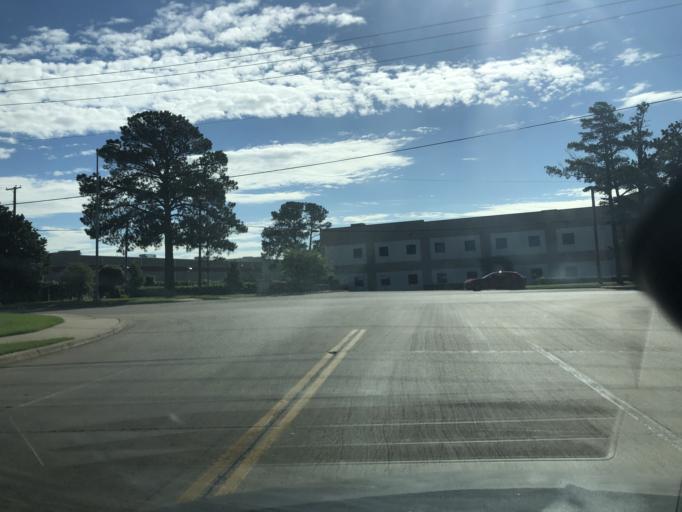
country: US
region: Texas
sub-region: Tarrant County
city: Euless
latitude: 32.8076
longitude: -97.0307
